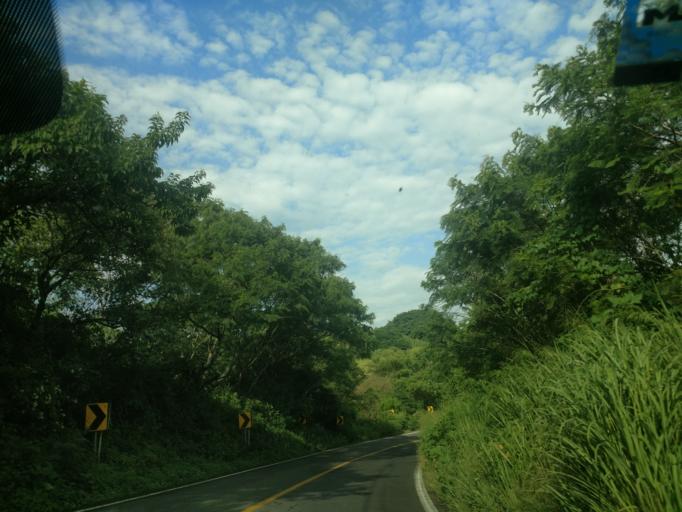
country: MX
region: Jalisco
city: Ameca
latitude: 20.5219
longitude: -104.1253
